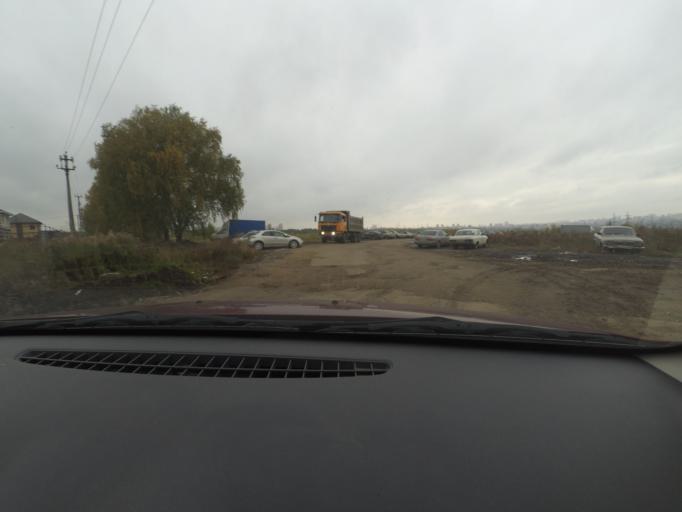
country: RU
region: Nizjnij Novgorod
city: Afonino
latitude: 56.2511
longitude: 44.0416
